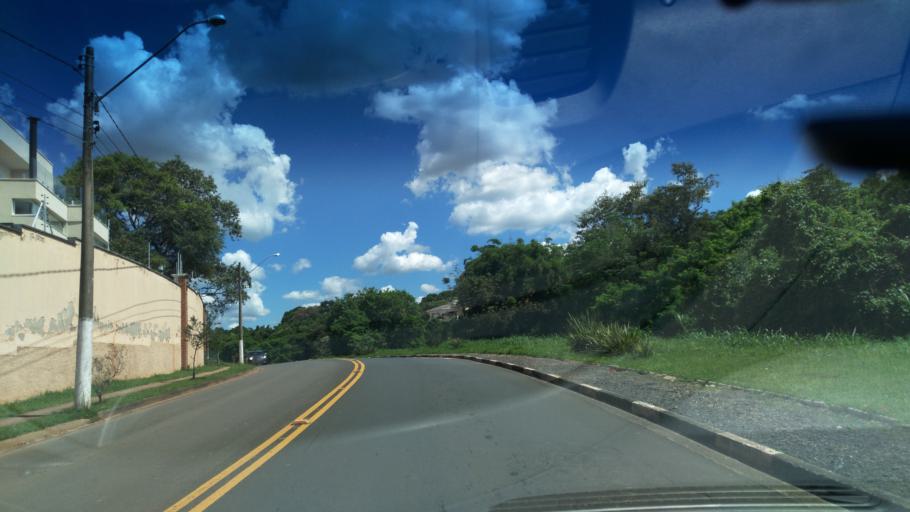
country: BR
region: Sao Paulo
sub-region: Valinhos
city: Valinhos
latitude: -22.9732
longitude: -47.0142
